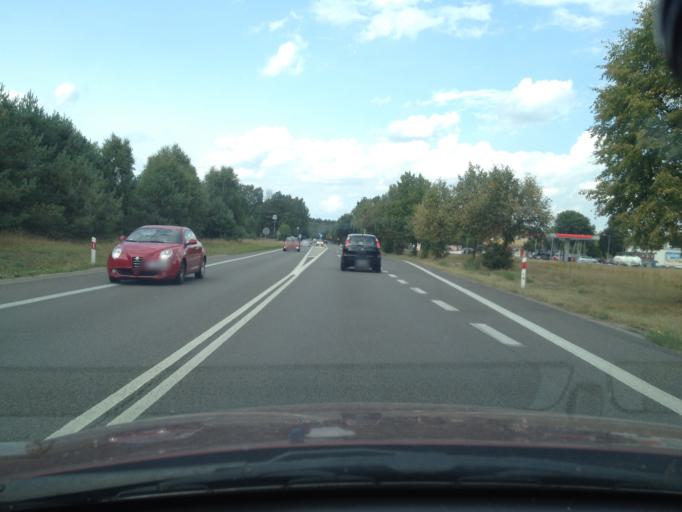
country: PL
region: West Pomeranian Voivodeship
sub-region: Powiat goleniowski
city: Przybiernow
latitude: 53.6769
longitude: 14.8127
